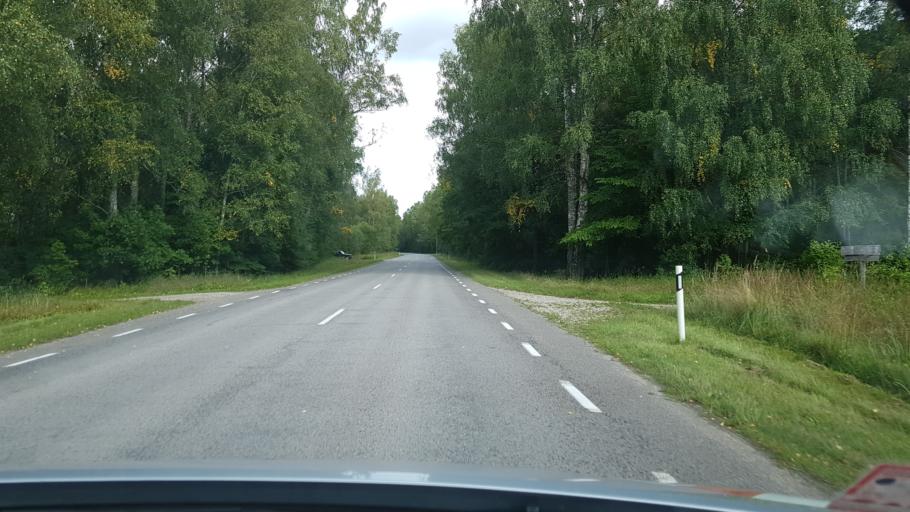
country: EE
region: Saare
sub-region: Kuressaare linn
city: Kuressaare
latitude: 58.3129
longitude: 22.2498
